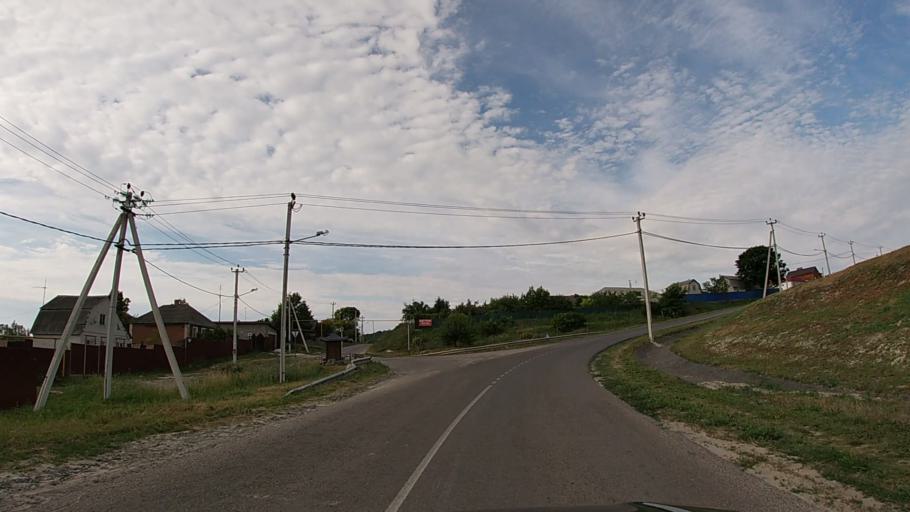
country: RU
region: Belgorod
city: Severnyy
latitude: 50.7068
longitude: 36.6005
